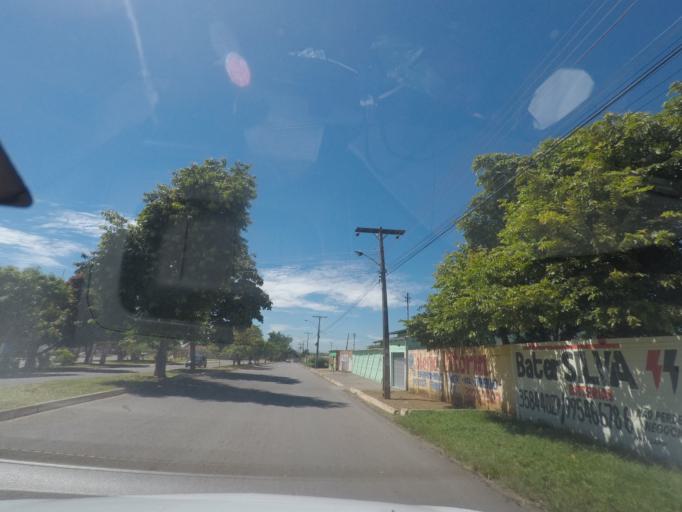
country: BR
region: Goias
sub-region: Aparecida De Goiania
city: Aparecida de Goiania
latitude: -16.7739
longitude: -49.3413
